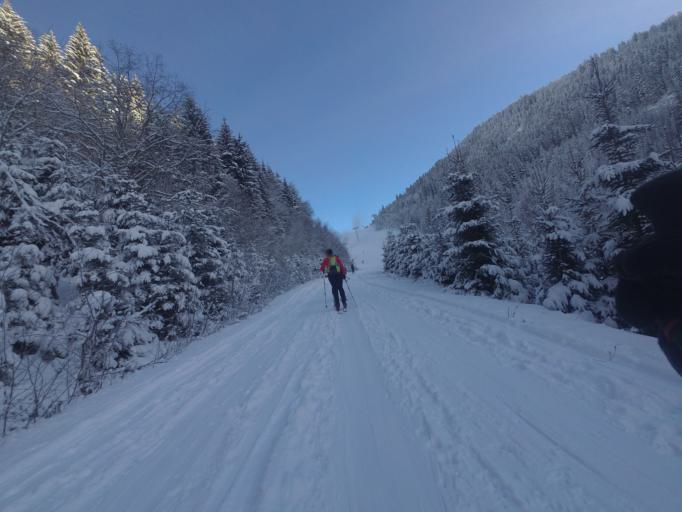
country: AT
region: Salzburg
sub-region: Politischer Bezirk Sankt Johann im Pongau
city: Sankt Johann im Pongau
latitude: 47.3175
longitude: 13.2129
